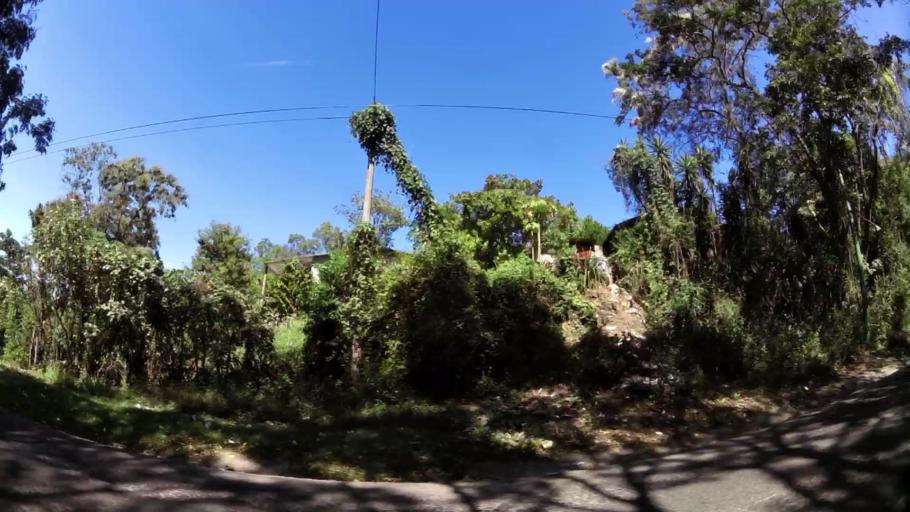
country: SV
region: Ahuachapan
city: Ahuachapan
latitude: 13.9457
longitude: -89.8219
